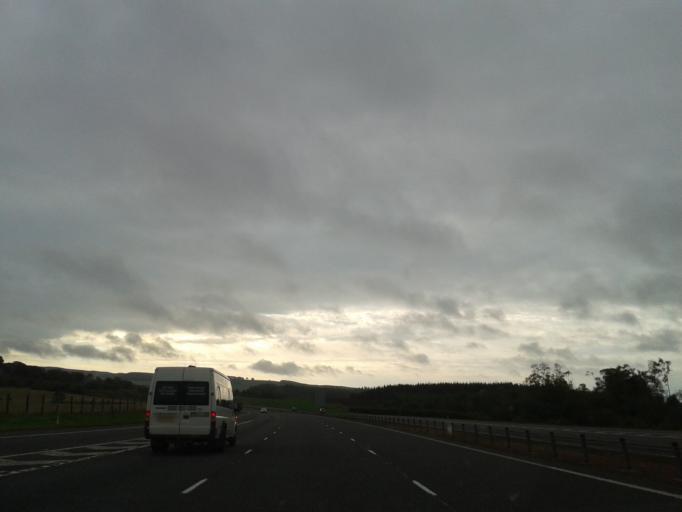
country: GB
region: Scotland
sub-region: Dumfries and Galloway
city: Lockerbie
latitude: 55.1020
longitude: -3.3457
